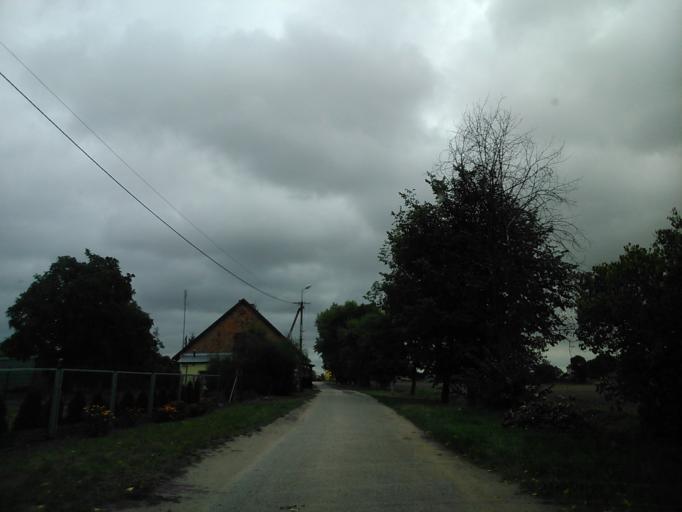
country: PL
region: Greater Poland Voivodeship
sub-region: Powiat koninski
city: Skulsk
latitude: 52.5781
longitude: 18.3763
